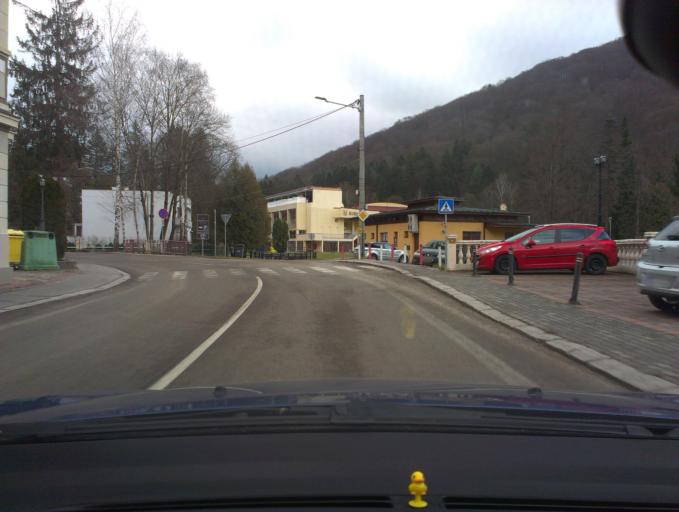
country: SK
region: Nitriansky
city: Trencianske Teplice
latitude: 48.9091
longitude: 18.1753
